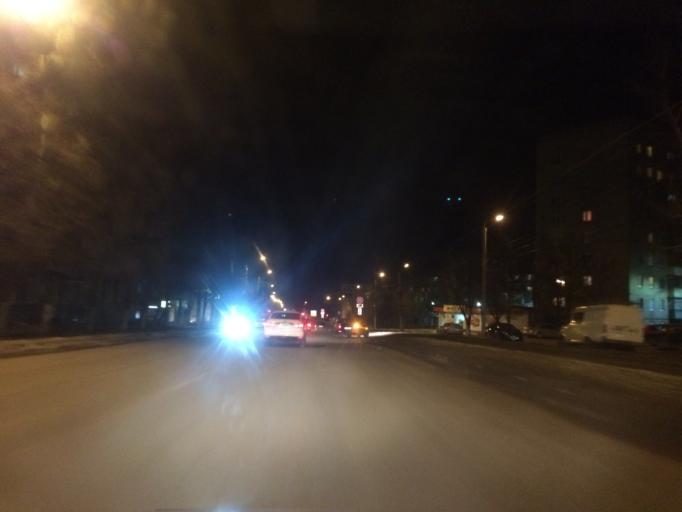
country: RU
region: Tula
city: Tula
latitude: 54.1883
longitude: 37.6924
